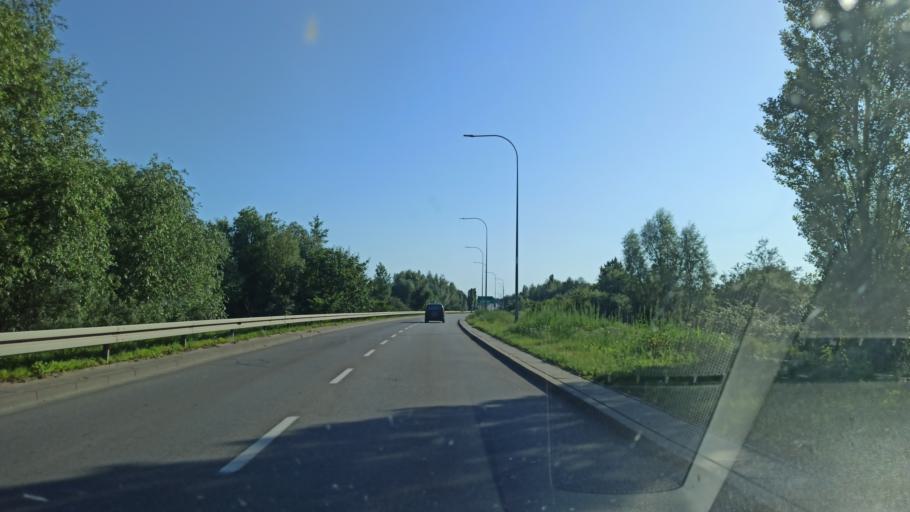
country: PL
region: Warmian-Masurian Voivodeship
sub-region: Powiat elblaski
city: Elblag
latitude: 54.1691
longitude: 19.3797
